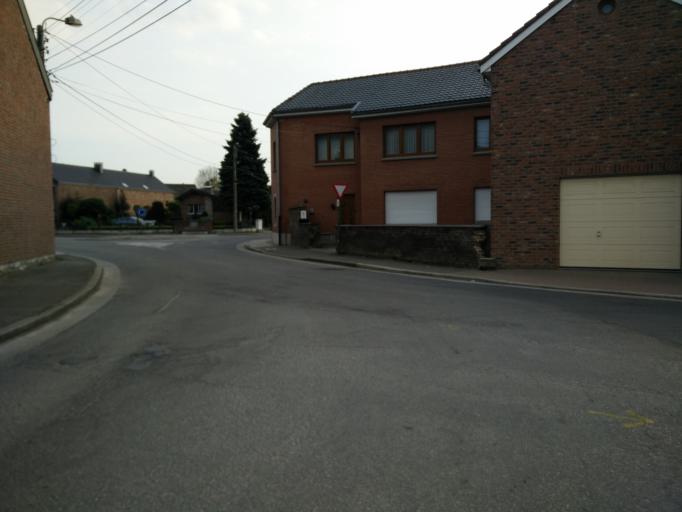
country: BE
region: Wallonia
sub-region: Province de Liege
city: Dalhem
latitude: 50.7374
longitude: 5.7675
